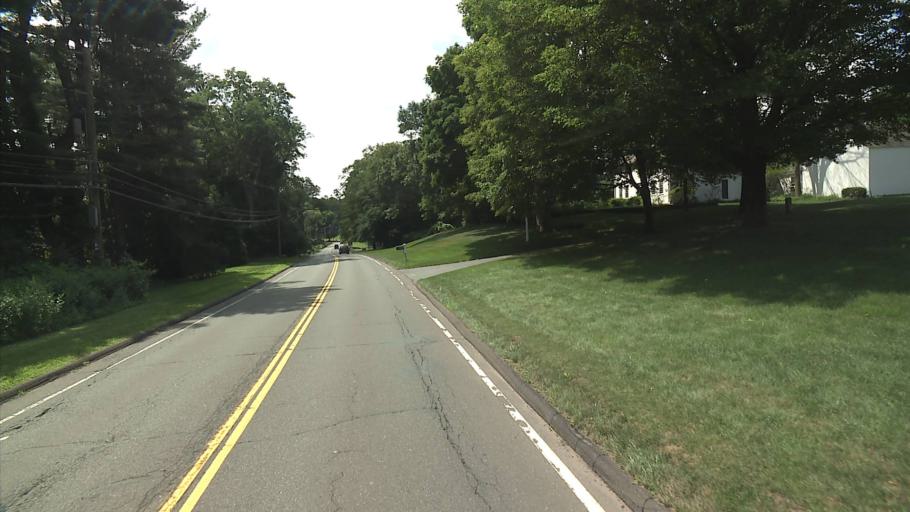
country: US
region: Connecticut
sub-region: Hartford County
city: Glastonbury Center
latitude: 41.6816
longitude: -72.5998
